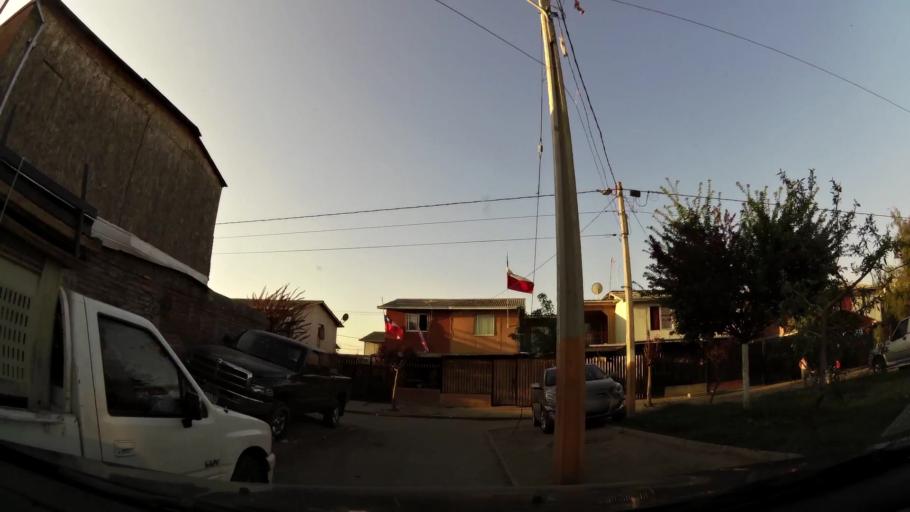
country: CL
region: Santiago Metropolitan
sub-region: Provincia de Maipo
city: San Bernardo
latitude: -33.5915
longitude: -70.6705
